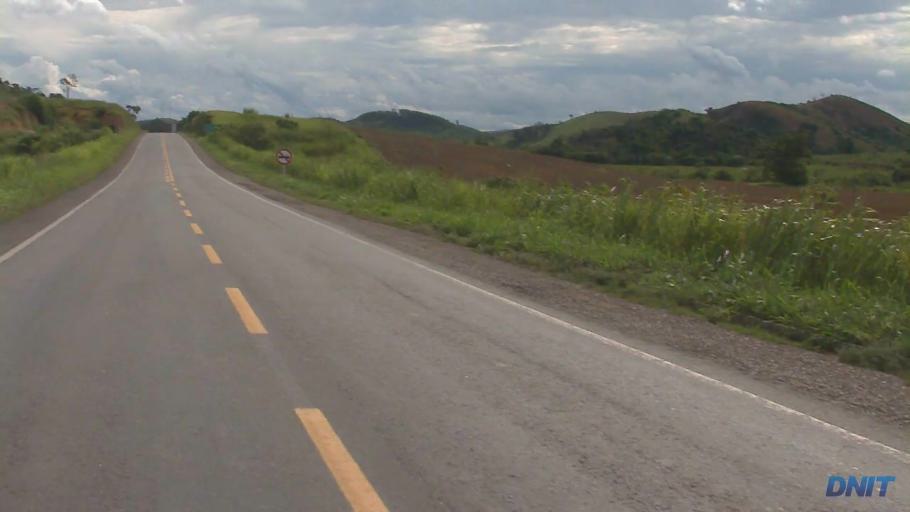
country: BR
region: Minas Gerais
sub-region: Belo Oriente
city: Belo Oriente
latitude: -19.1989
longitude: -42.2860
